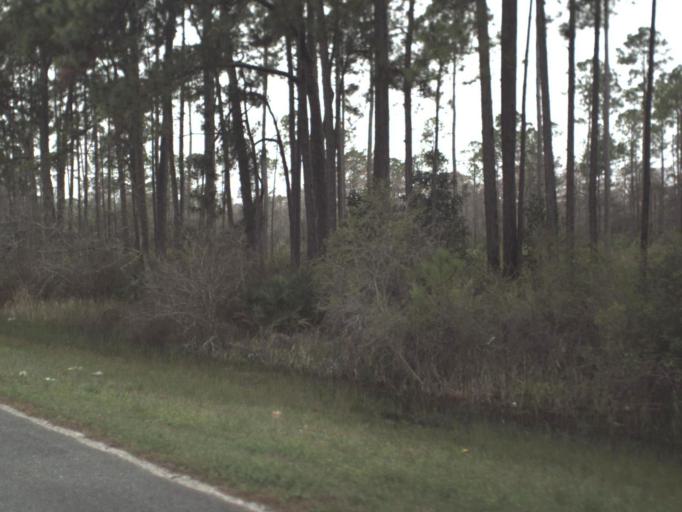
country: US
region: Florida
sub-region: Franklin County
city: Eastpoint
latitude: 29.7777
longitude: -84.8319
